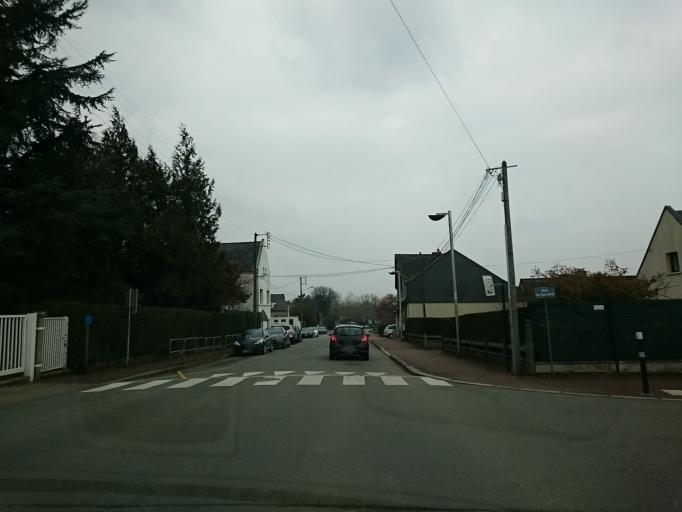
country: FR
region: Brittany
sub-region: Departement d'Ille-et-Vilaine
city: Bain-de-Bretagne
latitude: 47.8438
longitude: -1.6819
